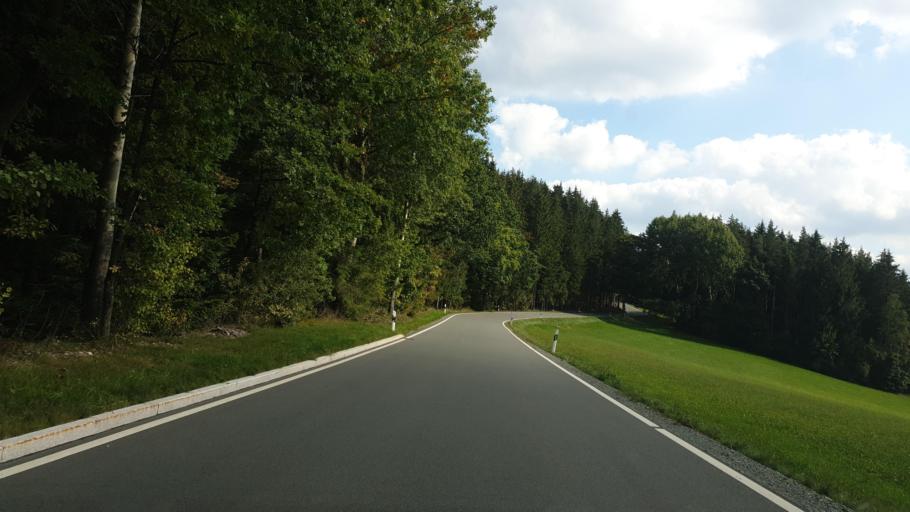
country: DE
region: Saxony
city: Rodewisch
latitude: 50.5107
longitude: 12.4441
